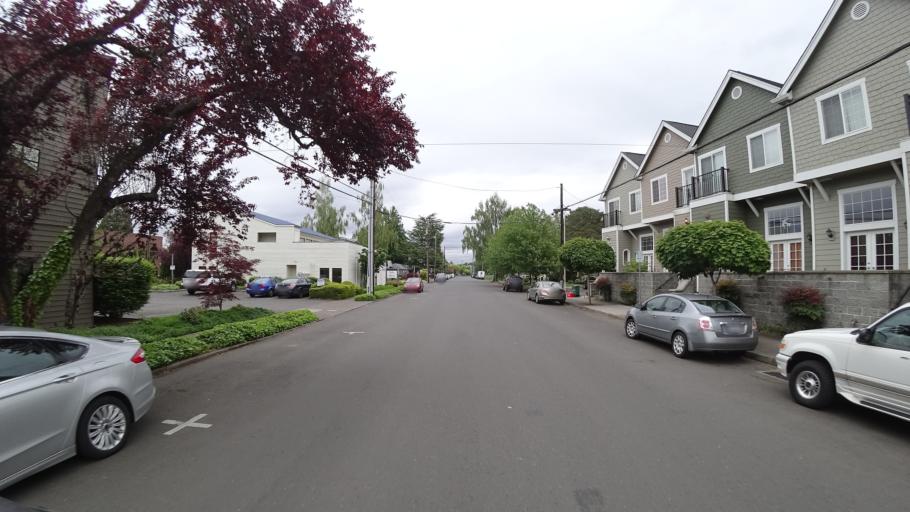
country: US
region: Oregon
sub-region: Washington County
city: Beaverton
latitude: 45.4854
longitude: -122.8032
